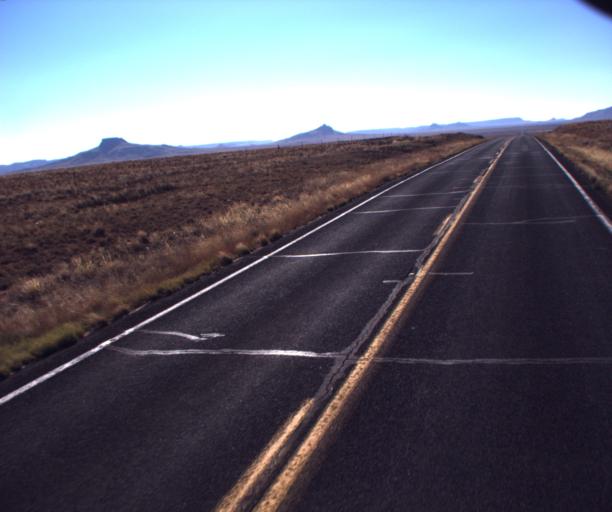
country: US
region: Arizona
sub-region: Navajo County
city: First Mesa
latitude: 35.6195
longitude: -110.4780
